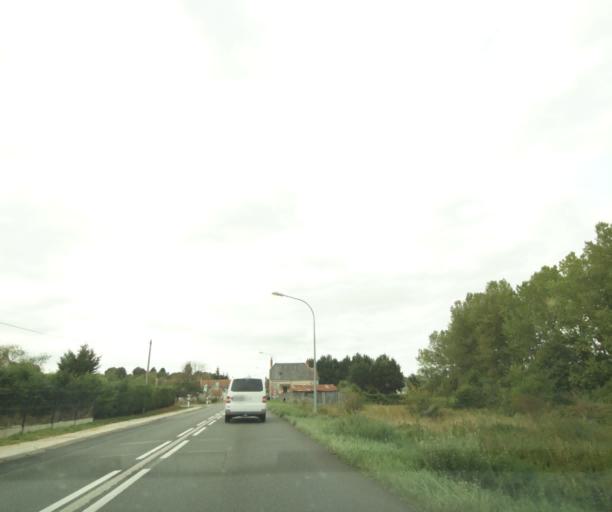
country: FR
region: Centre
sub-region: Departement d'Indre-et-Loire
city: Perrusson
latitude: 47.0580
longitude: 1.0853
